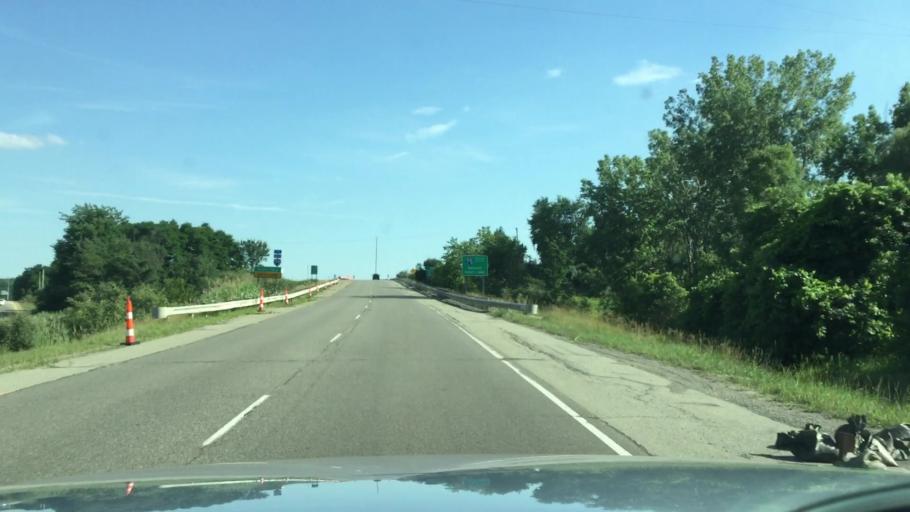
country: US
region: Michigan
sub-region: Genesee County
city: Grand Blanc
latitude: 42.8770
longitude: -83.5973
